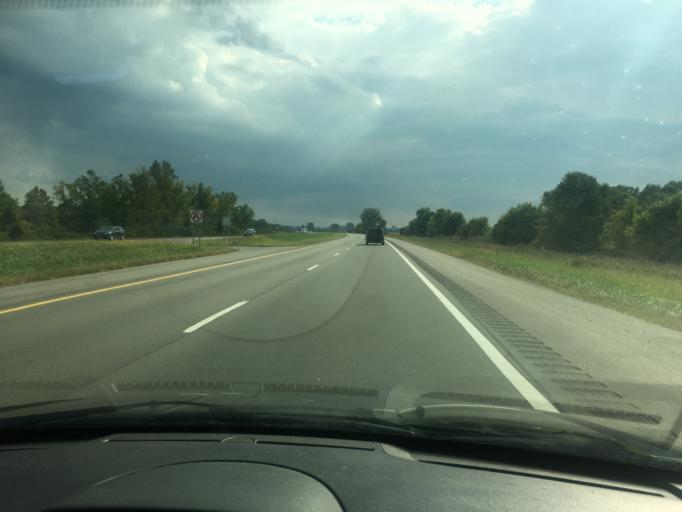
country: US
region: Ohio
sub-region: Clark County
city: Northridge
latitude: 40.0197
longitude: -83.8079
